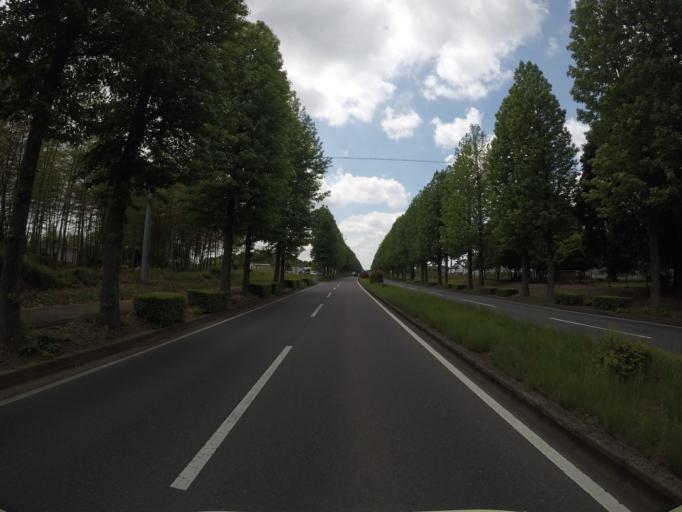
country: JP
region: Ibaraki
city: Naka
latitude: 36.0470
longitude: 140.1020
